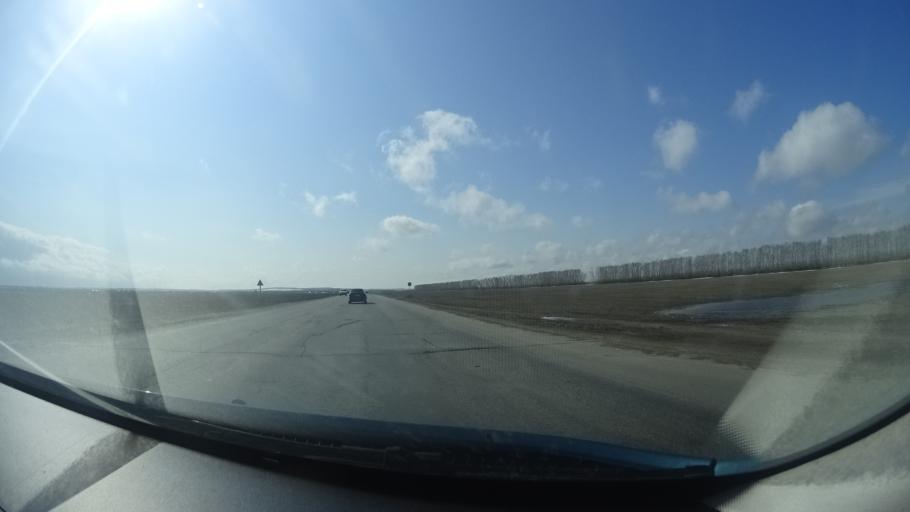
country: RU
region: Bashkortostan
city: Mikhaylovka
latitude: 54.9461
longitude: 55.7508
